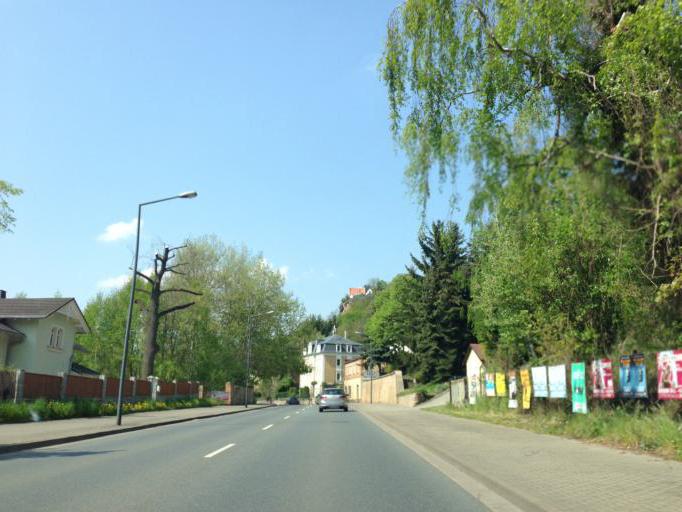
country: DE
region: Saxony
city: Bannewitz
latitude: 51.0226
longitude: 13.6947
